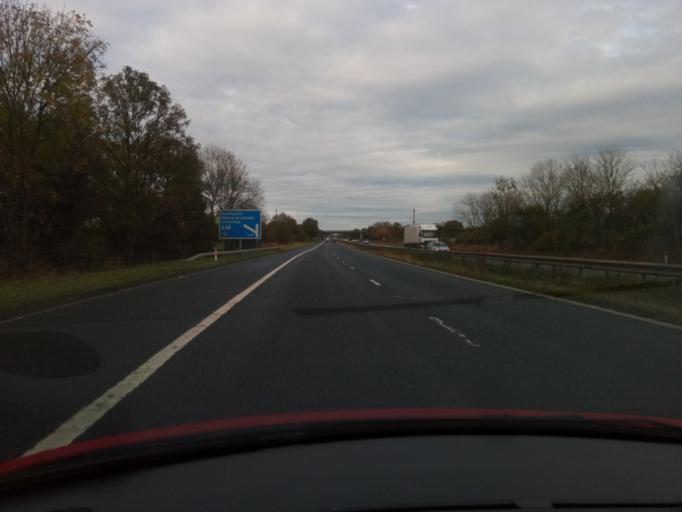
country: GB
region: England
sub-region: Darlington
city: High Coniscliffe
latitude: 54.5450
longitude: -1.6049
